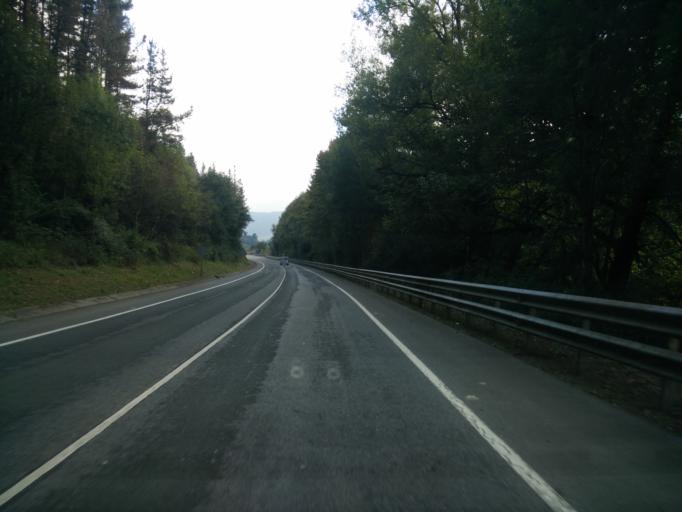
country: ES
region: Basque Country
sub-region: Bizkaia
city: Markina-Xemein
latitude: 43.2857
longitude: -2.4949
